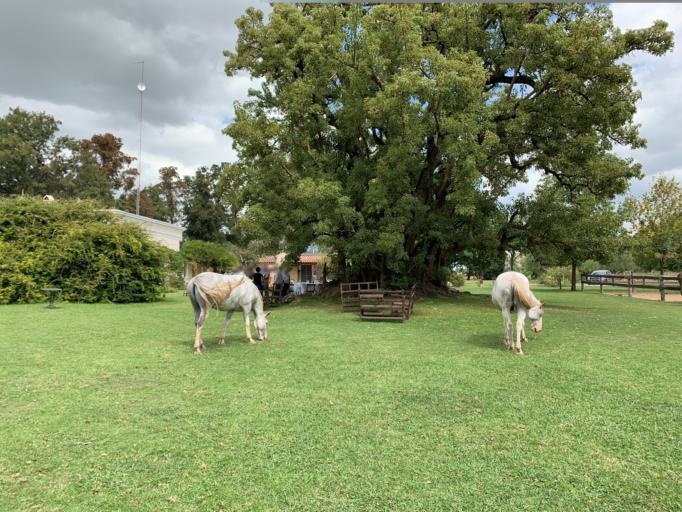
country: AR
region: Buenos Aires
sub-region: San Antonio de Areco
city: San Antonio de Areco
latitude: -34.1961
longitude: -59.3888
